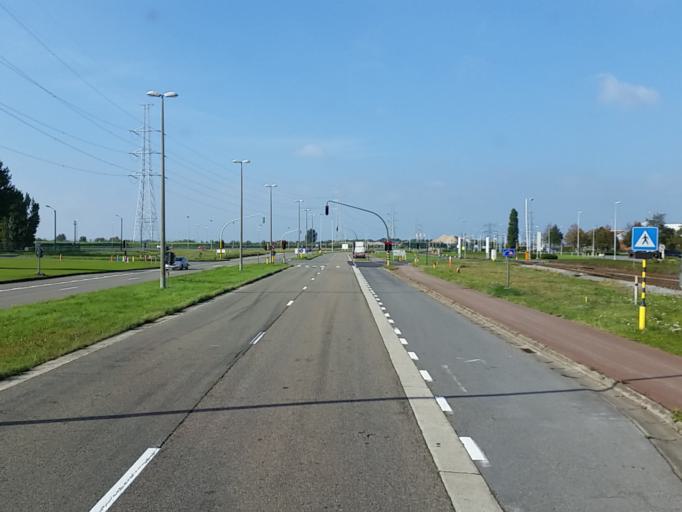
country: NL
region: North Brabant
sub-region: Gemeente Woensdrecht
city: Woensdrecht
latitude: 51.3598
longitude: 4.2580
